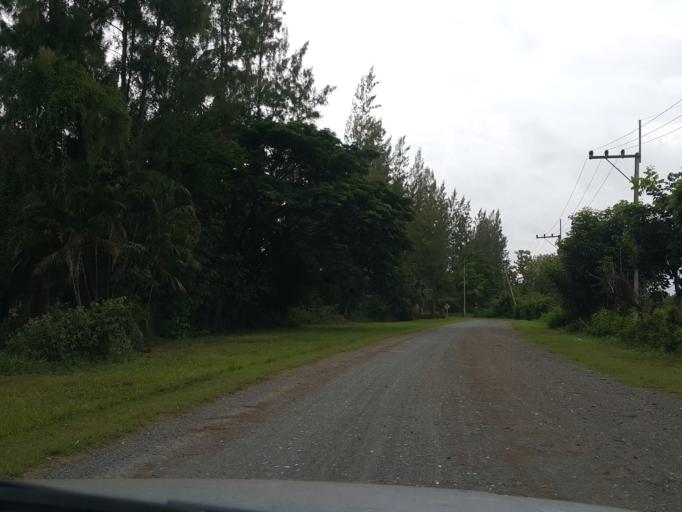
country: TH
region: Chiang Mai
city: San Kamphaeng
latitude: 18.8097
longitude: 99.1359
